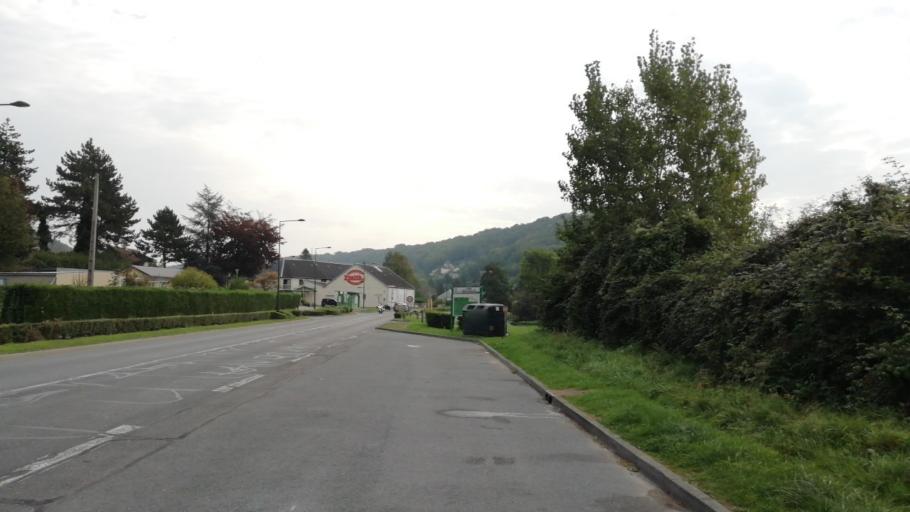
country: FR
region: Haute-Normandie
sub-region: Departement de la Seine-Maritime
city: Rogerville
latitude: 49.4950
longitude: 0.2823
